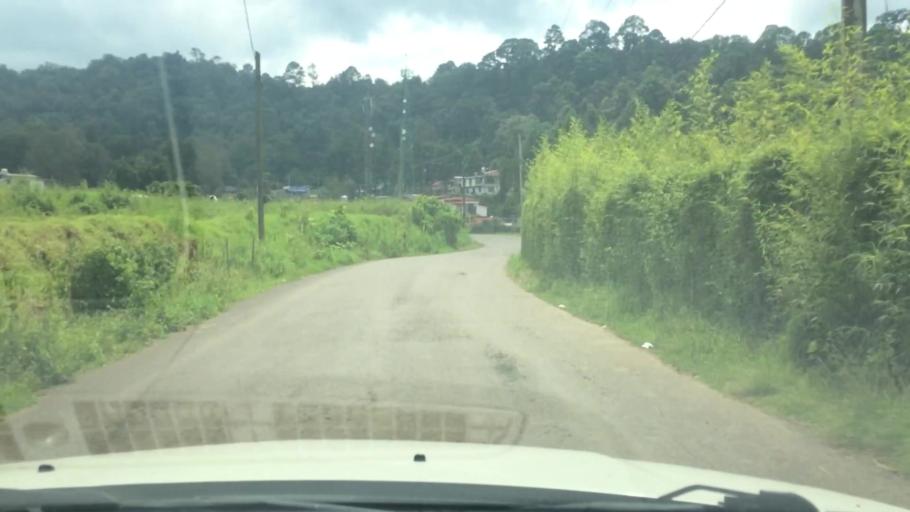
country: MX
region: Mexico
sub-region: Valle de Bravo
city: Cuadrilla de Dolores
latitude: 19.1517
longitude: -100.0581
